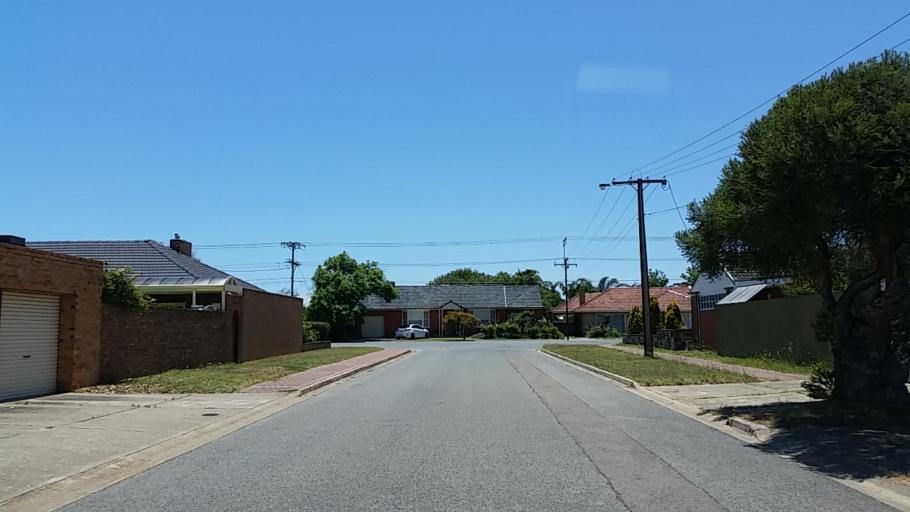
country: AU
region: South Australia
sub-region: Charles Sturt
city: Grange
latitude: -34.9025
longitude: 138.5013
